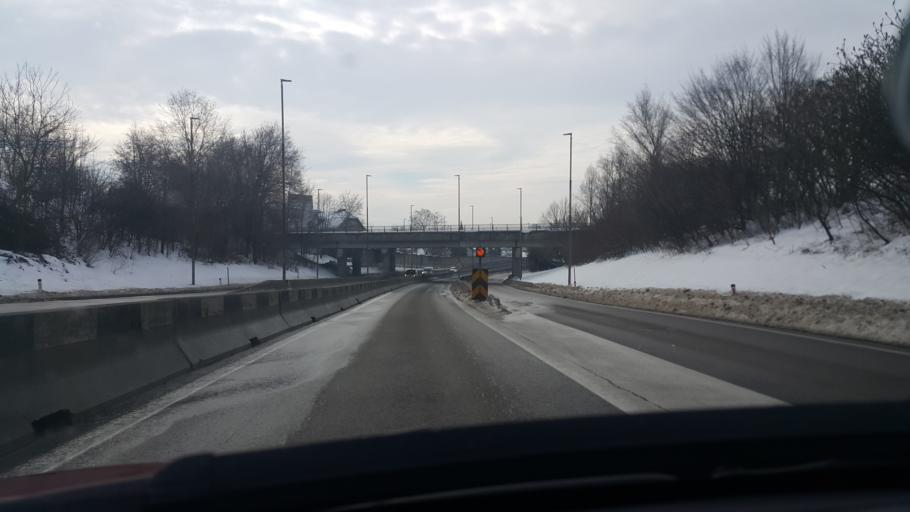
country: SI
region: Maribor
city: Maribor
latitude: 46.5640
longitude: 15.6622
